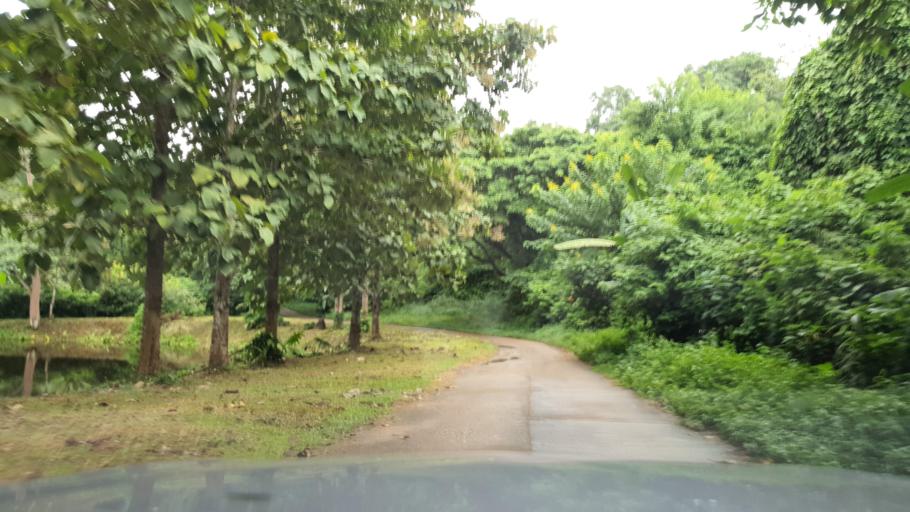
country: TH
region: Chiang Mai
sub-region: Amphoe Chiang Dao
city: Chiang Dao
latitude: 19.2829
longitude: 98.9631
